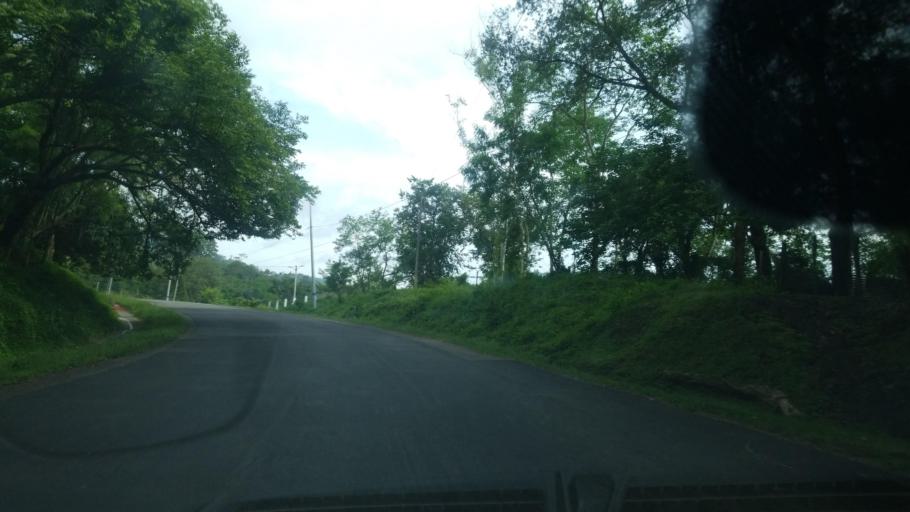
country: HN
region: Santa Barbara
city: Petoa
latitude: 15.2265
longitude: -88.2683
